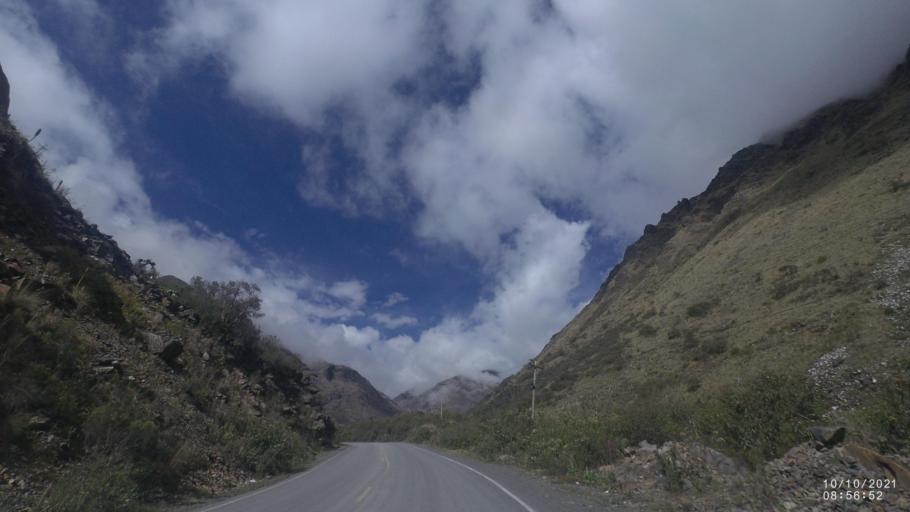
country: BO
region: La Paz
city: Quime
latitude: -16.9910
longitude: -67.2476
